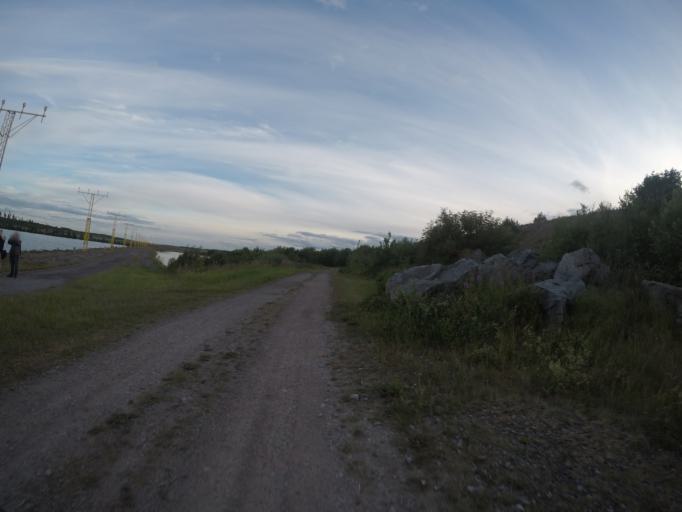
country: SE
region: Stockholm
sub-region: Sigtuna Kommun
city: Rosersberg
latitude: 59.6550
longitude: 17.9609
